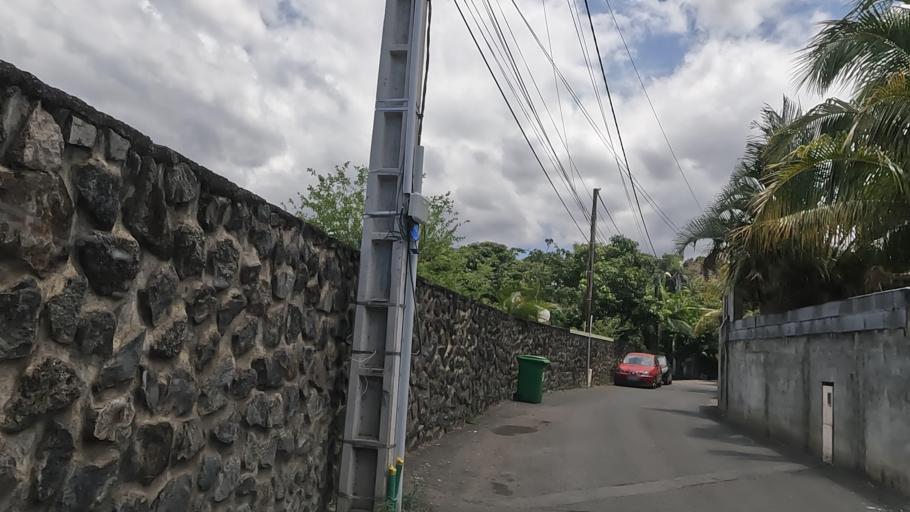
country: RE
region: Reunion
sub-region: Reunion
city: Saint-Louis
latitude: -21.2700
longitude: 55.4355
